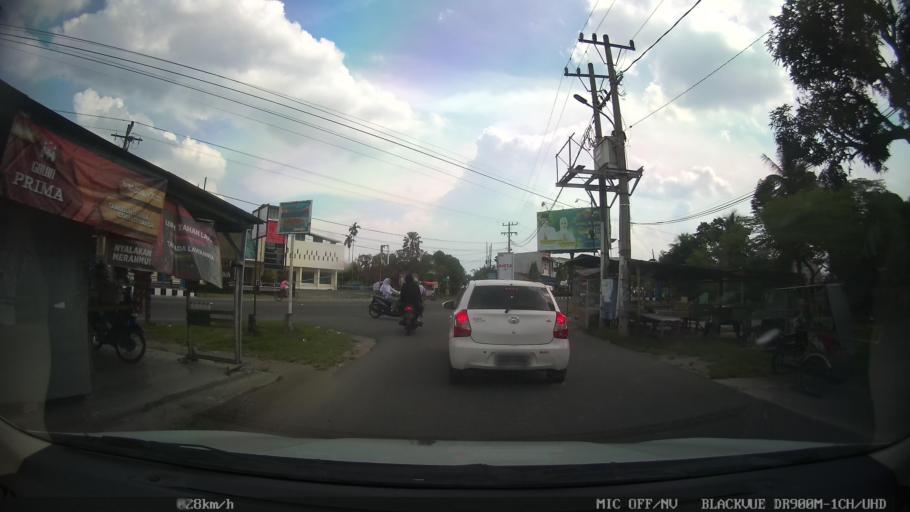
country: ID
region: North Sumatra
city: Binjai
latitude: 3.6215
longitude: 98.5005
